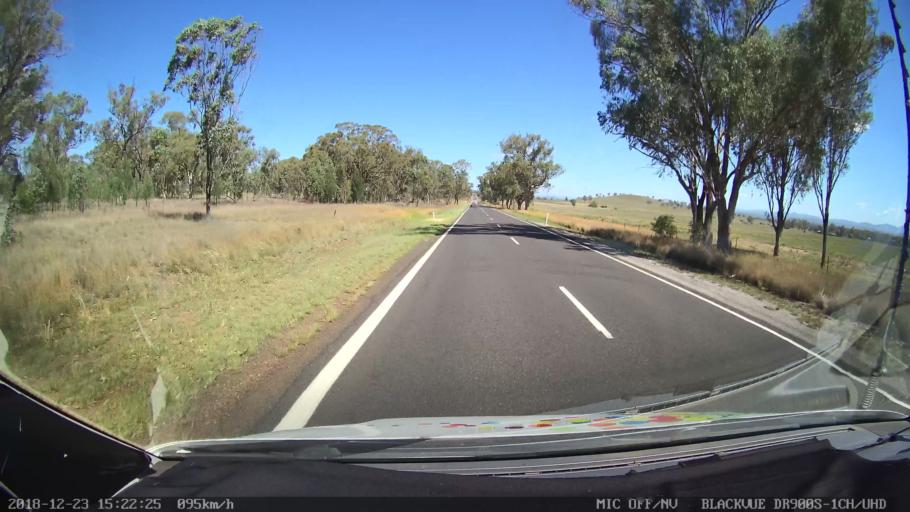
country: AU
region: New South Wales
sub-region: Tamworth Municipality
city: Manilla
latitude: -30.8680
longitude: 150.8047
